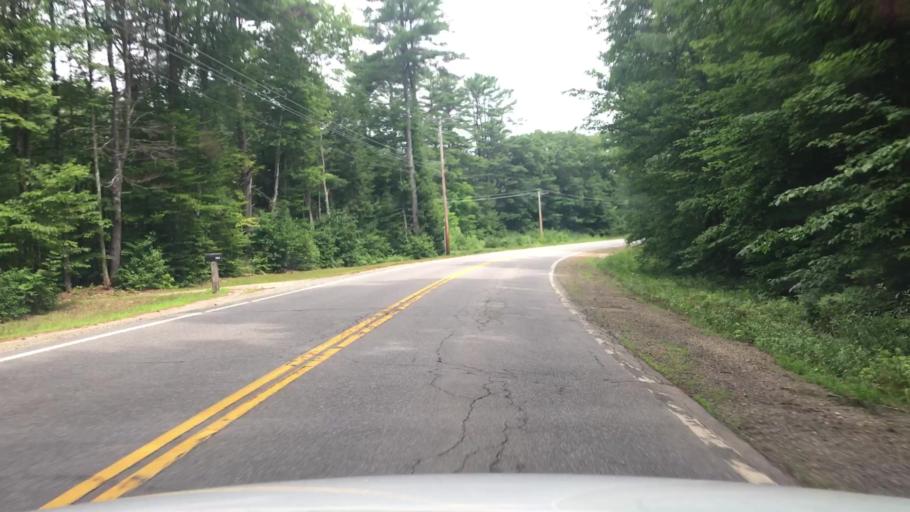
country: US
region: New Hampshire
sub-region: Grafton County
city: Plymouth
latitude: 43.7747
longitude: -71.6752
